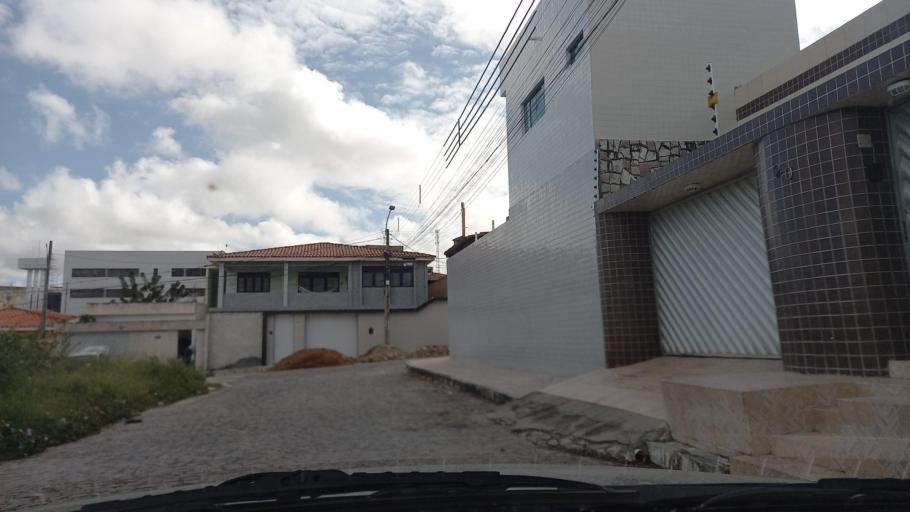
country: BR
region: Pernambuco
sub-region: Caruaru
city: Caruaru
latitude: -8.2902
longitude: -35.9837
